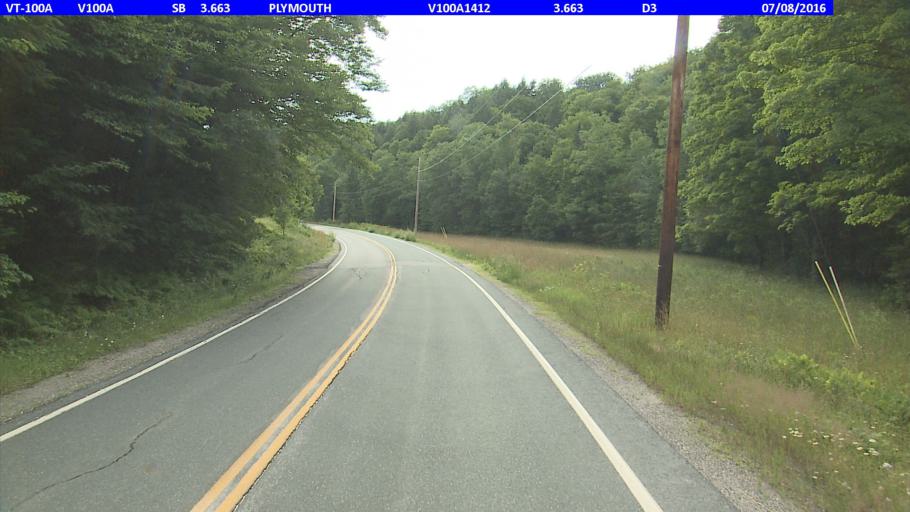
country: US
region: Vermont
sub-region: Windsor County
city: Woodstock
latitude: 43.5627
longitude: -72.6956
